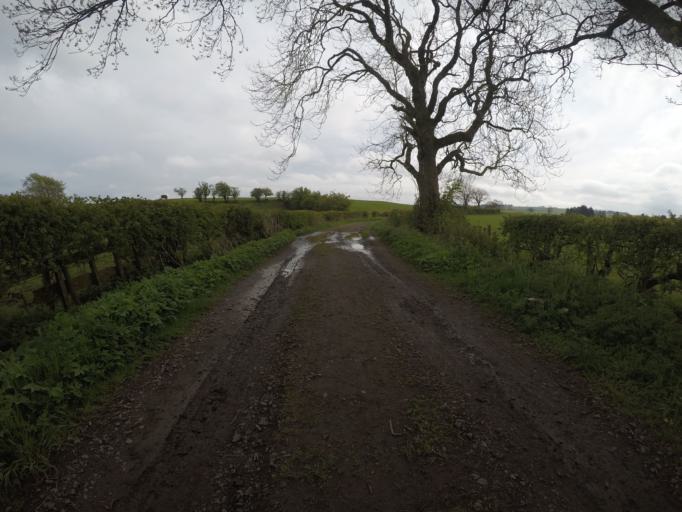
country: GB
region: Scotland
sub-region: East Renfrewshire
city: Newton Mearns
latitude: 55.7659
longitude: -4.3091
